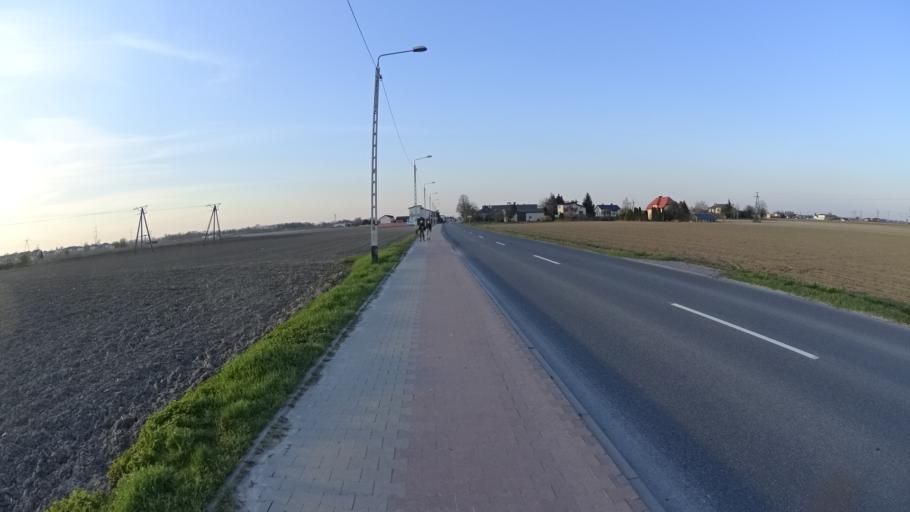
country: PL
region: Masovian Voivodeship
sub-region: Powiat warszawski zachodni
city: Ozarow Mazowiecki
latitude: 52.2191
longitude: 20.8124
